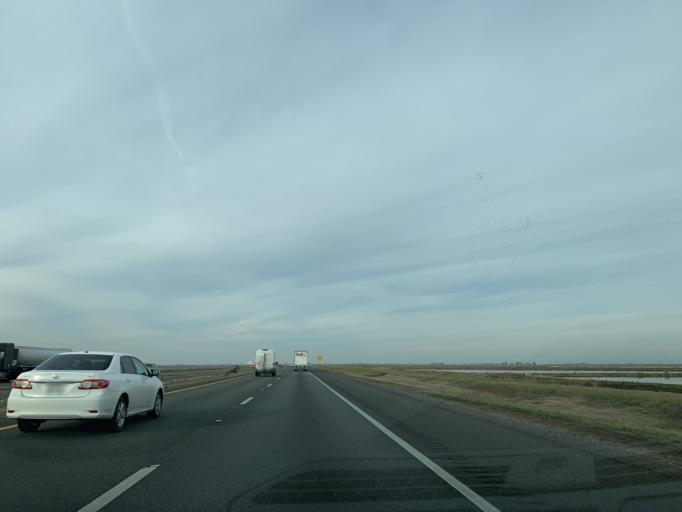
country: US
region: California
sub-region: Sacramento County
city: Elverta
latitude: 38.7672
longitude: -121.5434
